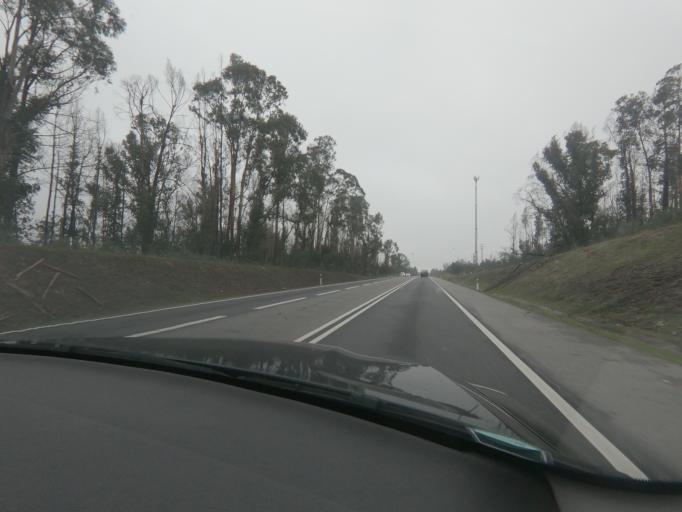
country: PT
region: Viseu
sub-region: Concelho de Tondela
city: Tondela
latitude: 40.5623
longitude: -8.0509
